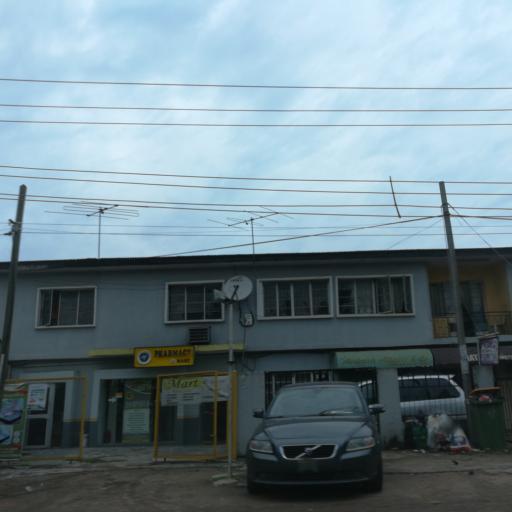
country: NG
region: Lagos
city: Ikeja
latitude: 6.5952
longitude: 3.3472
